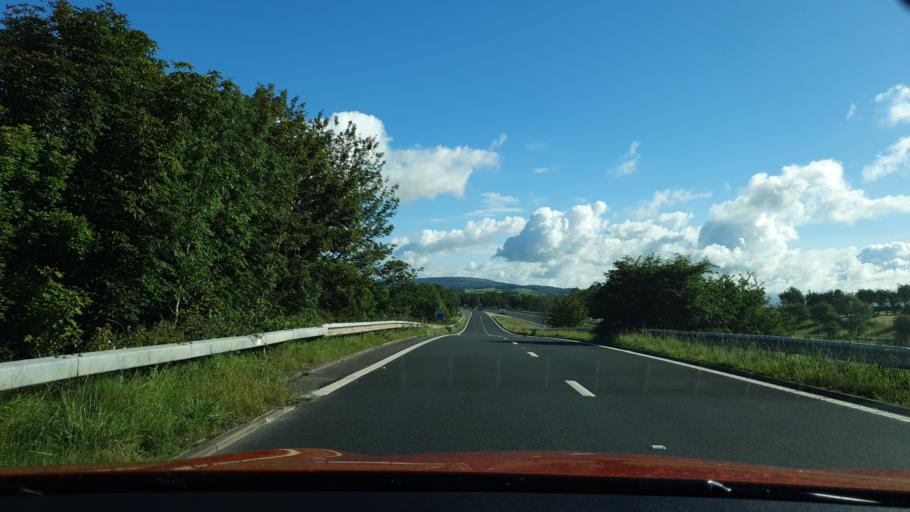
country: GB
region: England
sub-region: Lancashire
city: Carnforth
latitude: 54.1296
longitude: -2.7493
